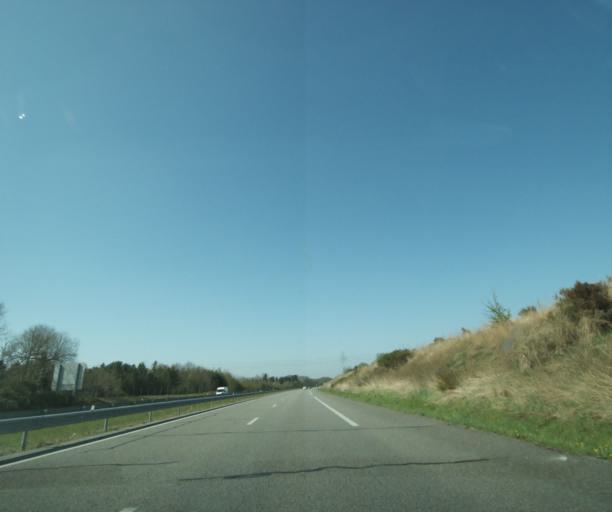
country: FR
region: Centre
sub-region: Departement du Loiret
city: Nogent-sur-Vernisson
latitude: 47.7464
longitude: 2.7243
